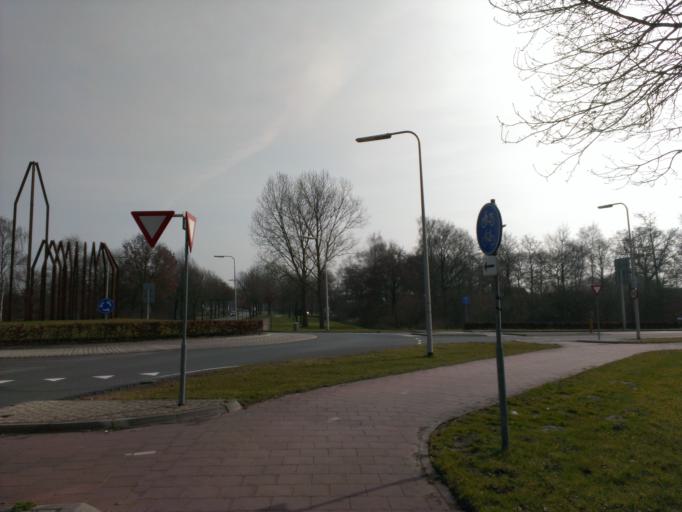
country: NL
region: Drenthe
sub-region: Gemeente Hoogeveen
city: Hoogeveen
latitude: 52.7390
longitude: 6.4849
